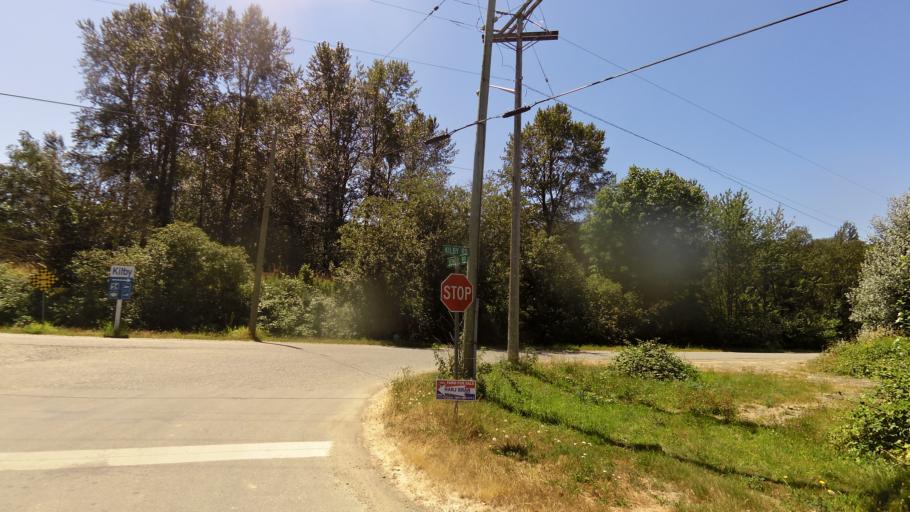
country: CA
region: British Columbia
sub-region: Fraser Valley Regional District
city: Chilliwack
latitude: 49.2356
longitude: -121.9460
